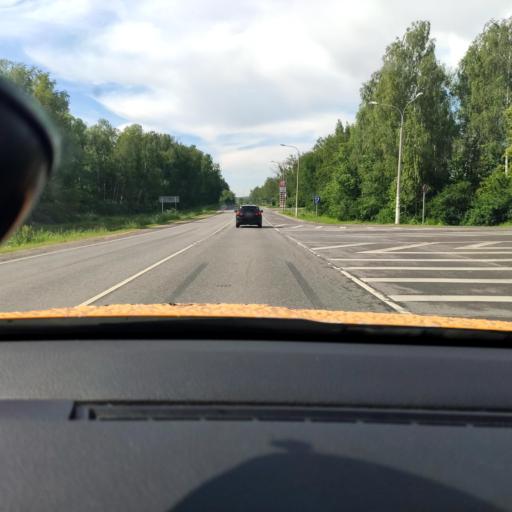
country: RU
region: Moskovskaya
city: Stupino
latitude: 54.9345
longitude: 38.0424
